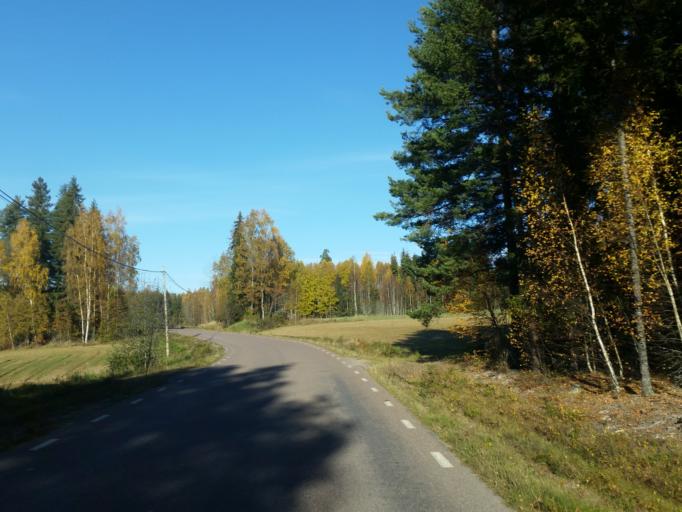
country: SE
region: Dalarna
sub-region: Borlange Kommun
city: Ornas
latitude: 60.4500
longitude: 15.6200
